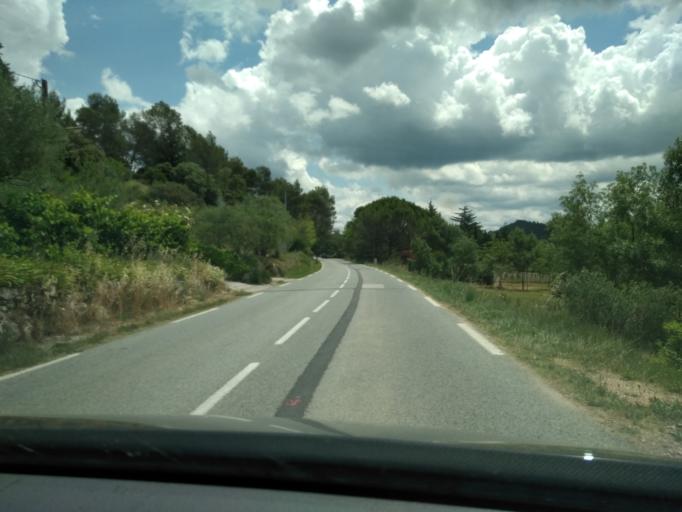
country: FR
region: Provence-Alpes-Cote d'Azur
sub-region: Departement du Var
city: Le Val
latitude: 43.4463
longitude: 6.0901
